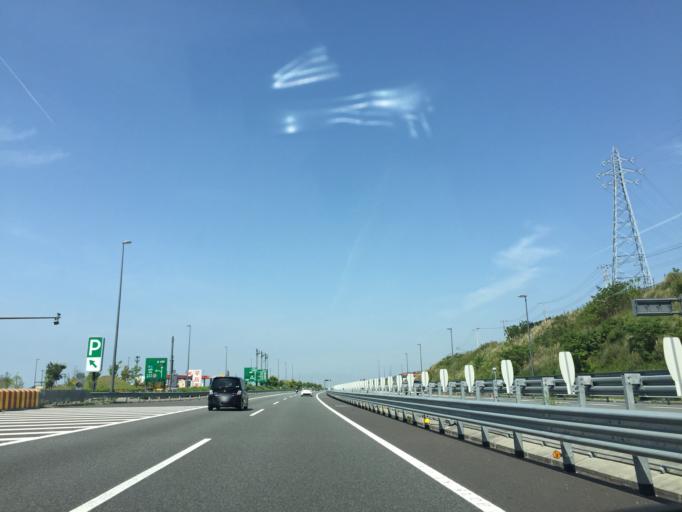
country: JP
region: Shizuoka
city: Numazu
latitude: 35.1534
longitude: 138.8138
